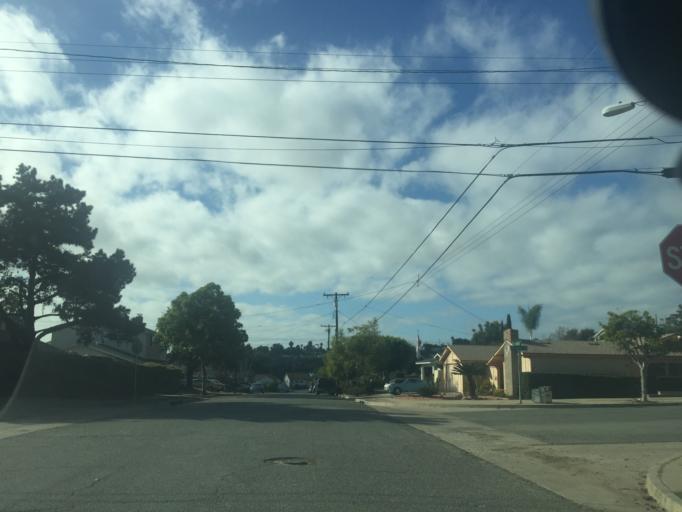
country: US
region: California
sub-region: San Diego County
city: San Diego
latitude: 32.7820
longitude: -117.1504
